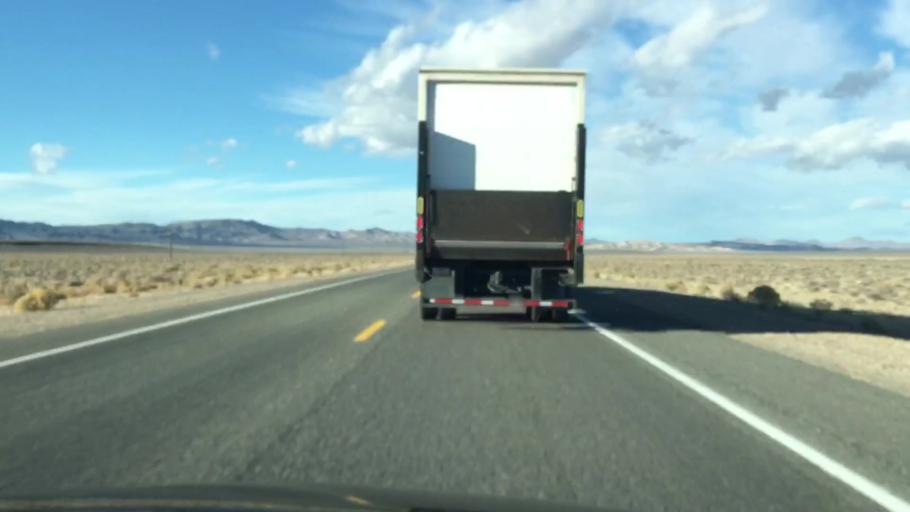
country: US
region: Nevada
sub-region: Esmeralda County
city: Goldfield
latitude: 37.4348
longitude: -117.1623
